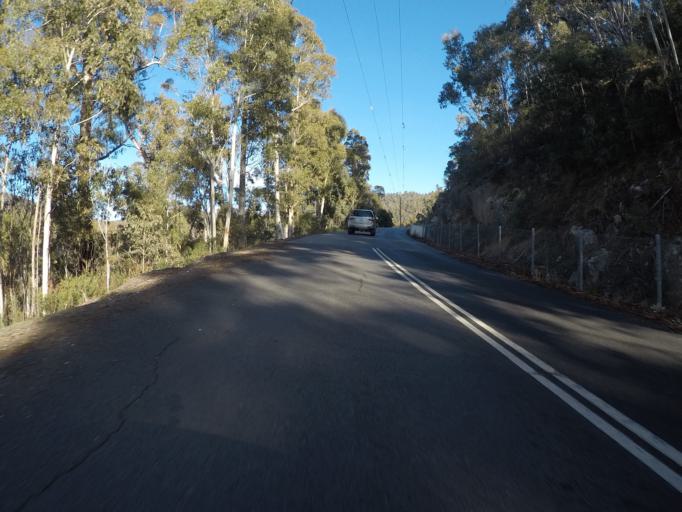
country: AU
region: Australian Capital Territory
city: Macarthur
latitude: -35.4919
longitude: 148.9310
